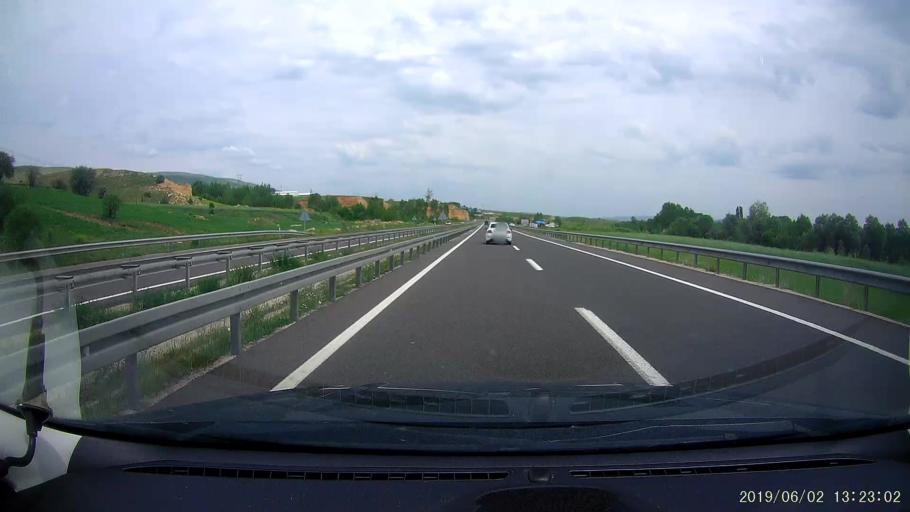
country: TR
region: Cankiri
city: Cerkes
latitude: 40.8250
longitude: 32.8106
